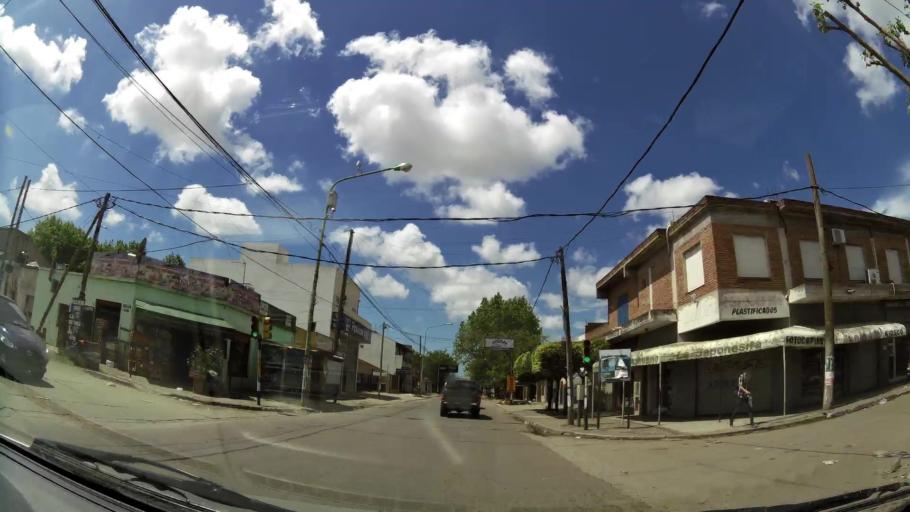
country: AR
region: Buenos Aires
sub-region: Partido de Quilmes
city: Quilmes
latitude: -34.8094
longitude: -58.2560
